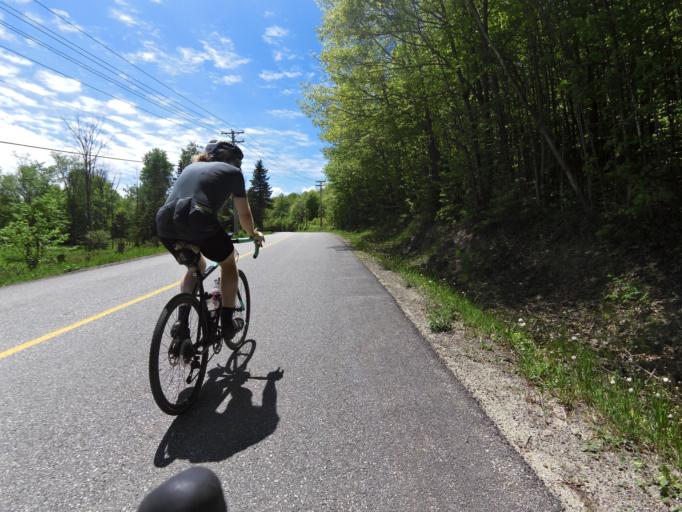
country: CA
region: Quebec
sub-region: Outaouais
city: Wakefield
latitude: 45.6712
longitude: -75.9452
